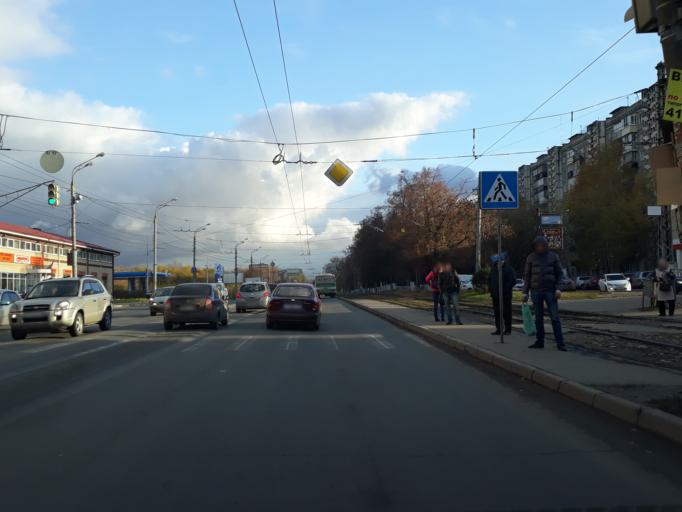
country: RU
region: Nizjnij Novgorod
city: Neklyudovo
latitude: 56.3414
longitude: 43.8782
